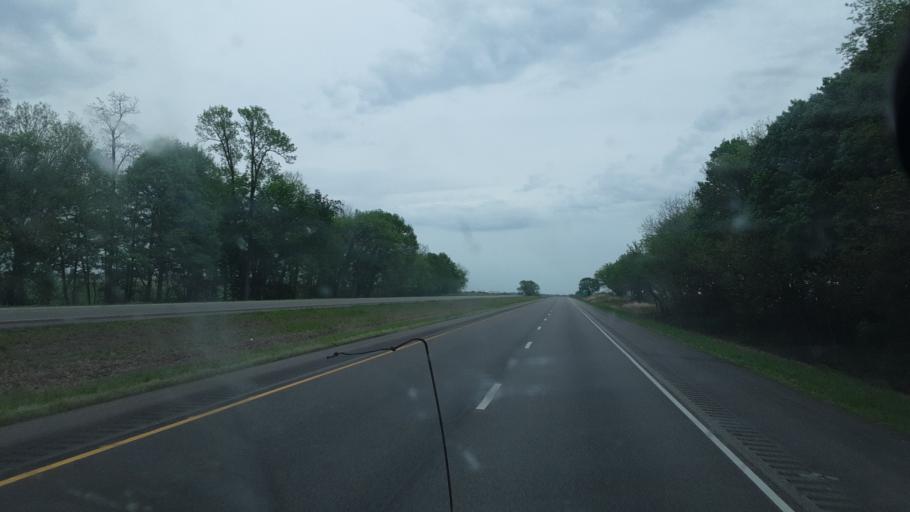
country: US
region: Indiana
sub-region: Posey County
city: Poseyville
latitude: 38.1842
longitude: -87.8037
